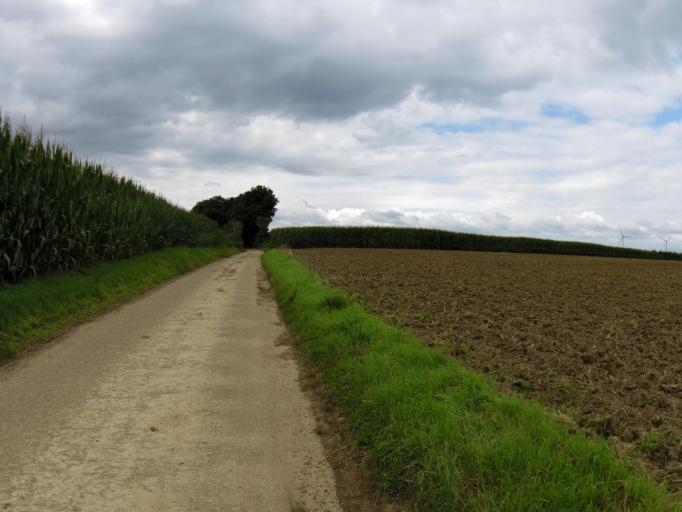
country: BE
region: Flanders
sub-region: Provincie Limburg
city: Riemst
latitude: 50.7899
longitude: 5.5470
